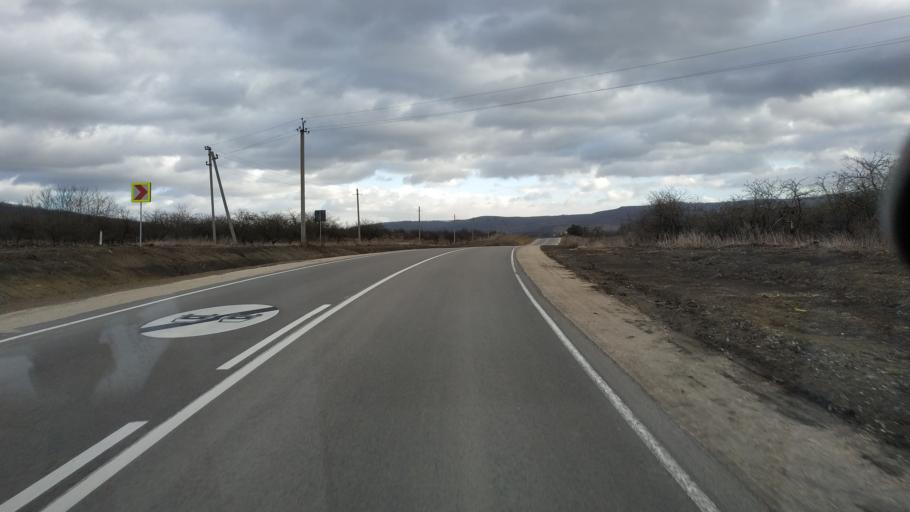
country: MD
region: Calarasi
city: Calarasi
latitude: 47.2698
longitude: 28.2265
